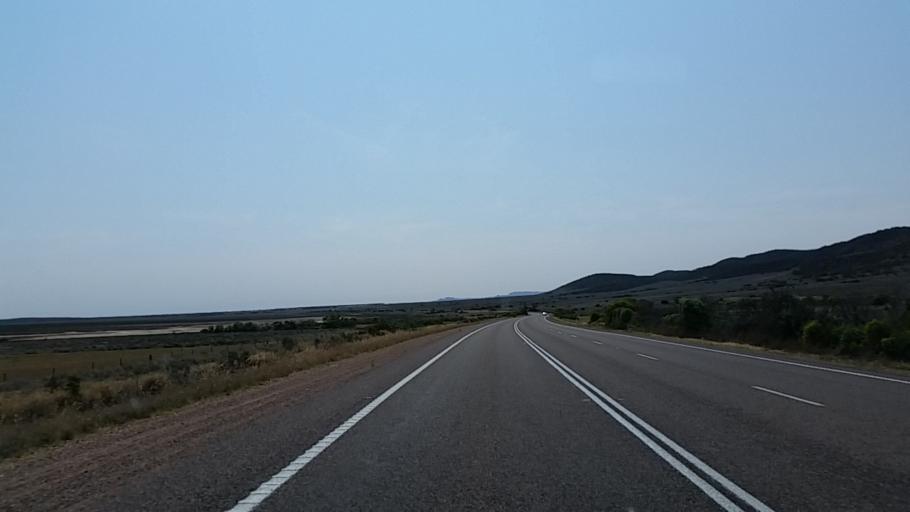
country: AU
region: South Australia
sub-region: Port Augusta
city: Port Augusta
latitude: -32.7775
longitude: 137.9540
